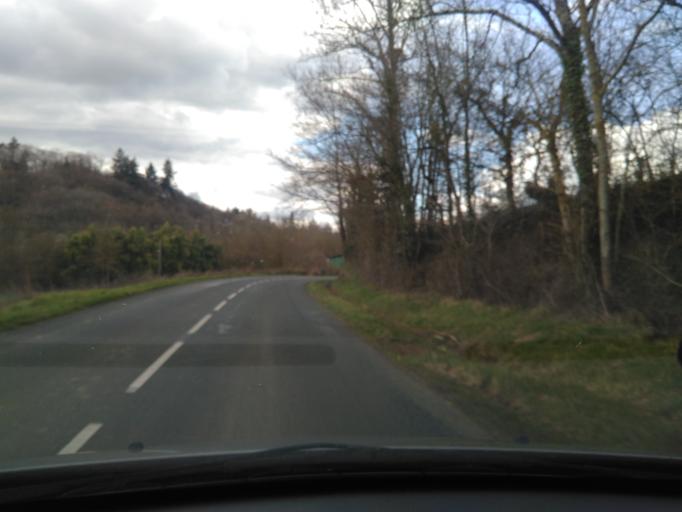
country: FR
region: Pays de la Loire
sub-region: Departement de la Vendee
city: Sainte-Cecile
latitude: 46.6884
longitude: -1.1140
